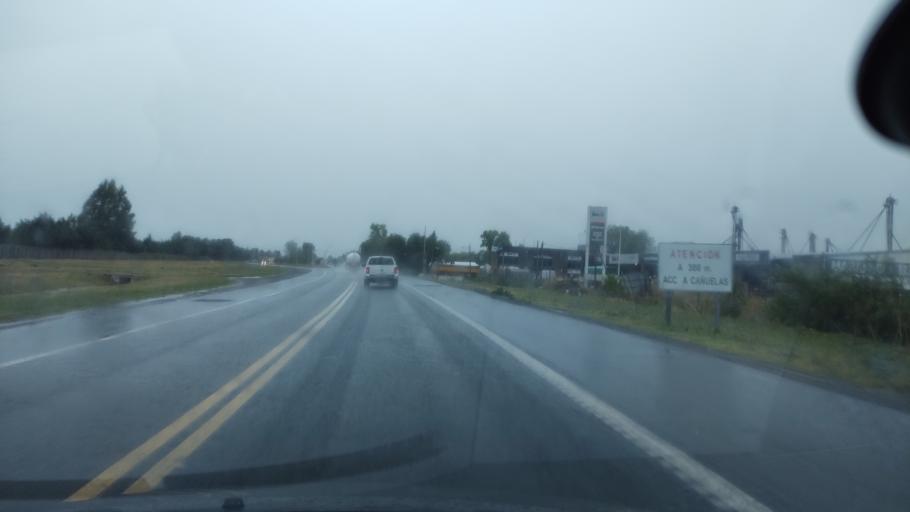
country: AR
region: Buenos Aires
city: Canuelas
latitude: -35.0519
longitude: -58.7748
